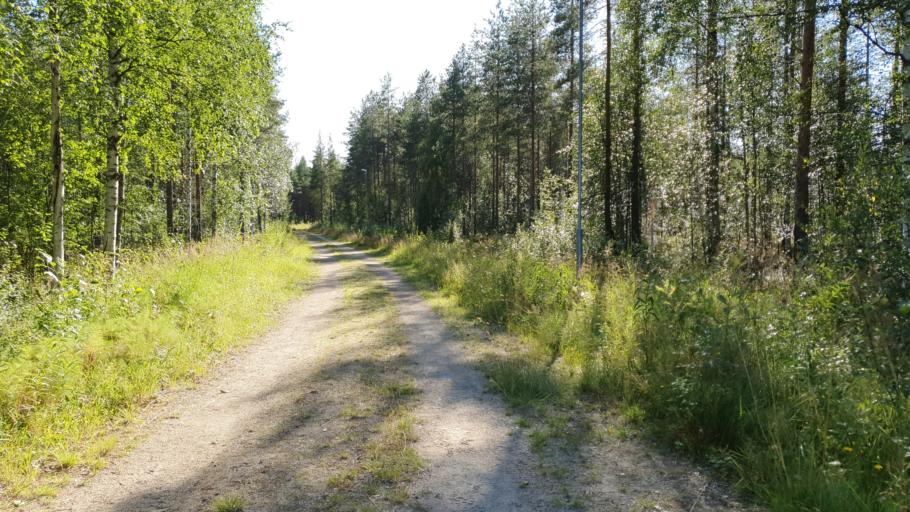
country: FI
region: Kainuu
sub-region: Kehys-Kainuu
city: Kuhmo
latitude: 64.1145
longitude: 29.5088
